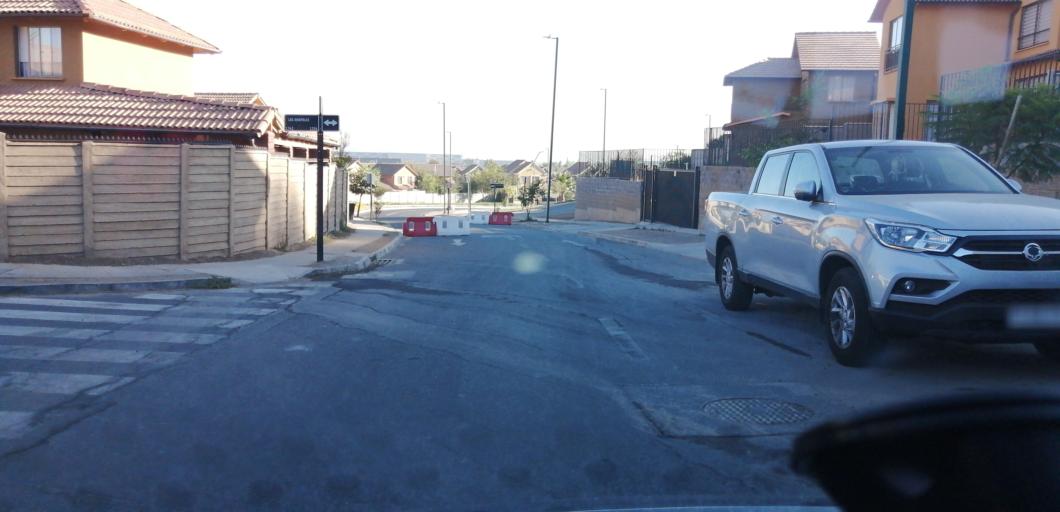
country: CL
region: Santiago Metropolitan
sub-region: Provincia de Santiago
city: Lo Prado
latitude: -33.4535
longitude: -70.8448
